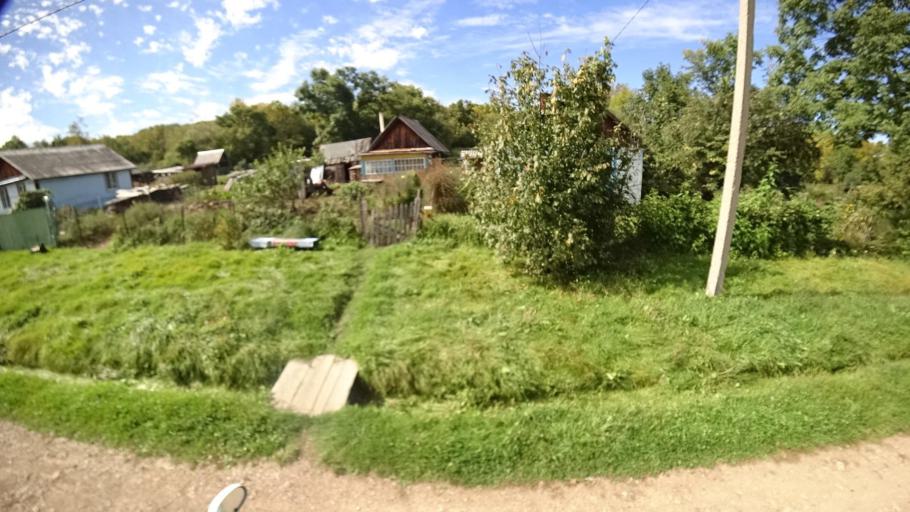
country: RU
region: Primorskiy
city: Yakovlevka
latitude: 44.3953
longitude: 133.5978
